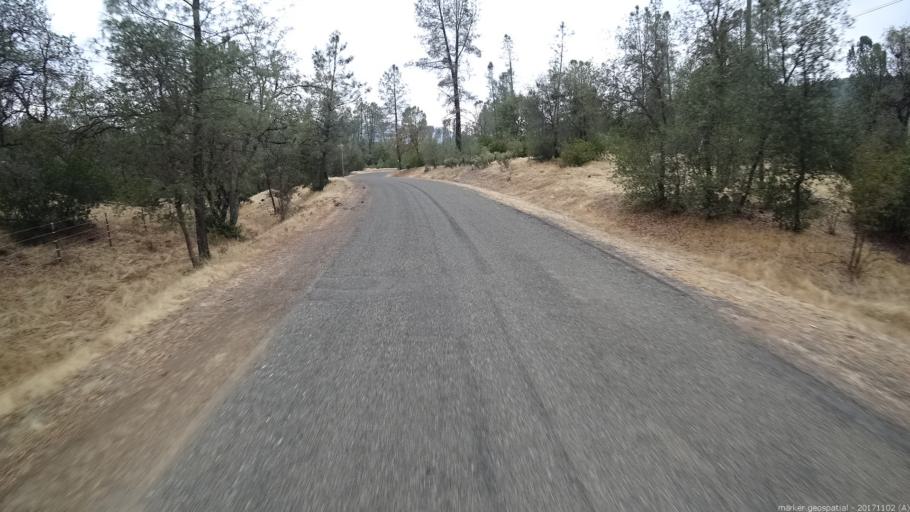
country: US
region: California
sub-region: Shasta County
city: Central Valley (historical)
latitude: 40.6595
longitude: -122.4349
